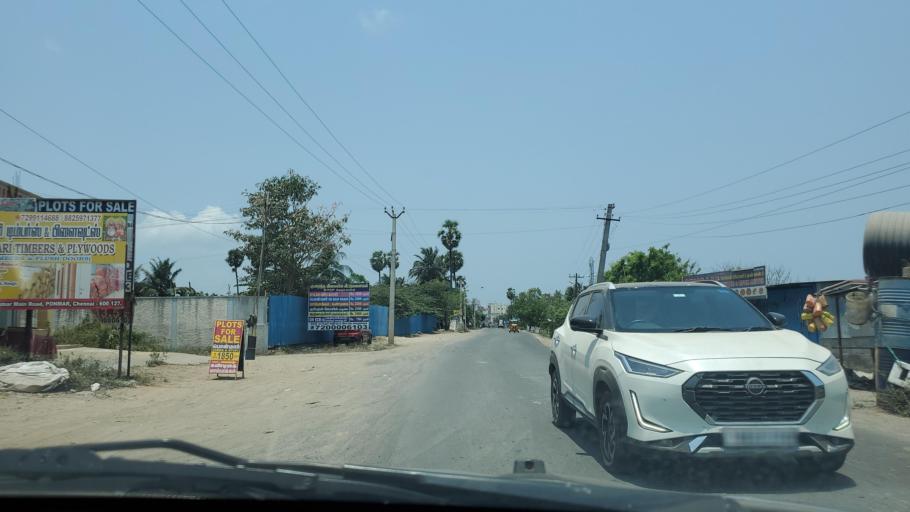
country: IN
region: Tamil Nadu
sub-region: Kancheepuram
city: Vengavasal
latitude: 12.8537
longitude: 80.1713
